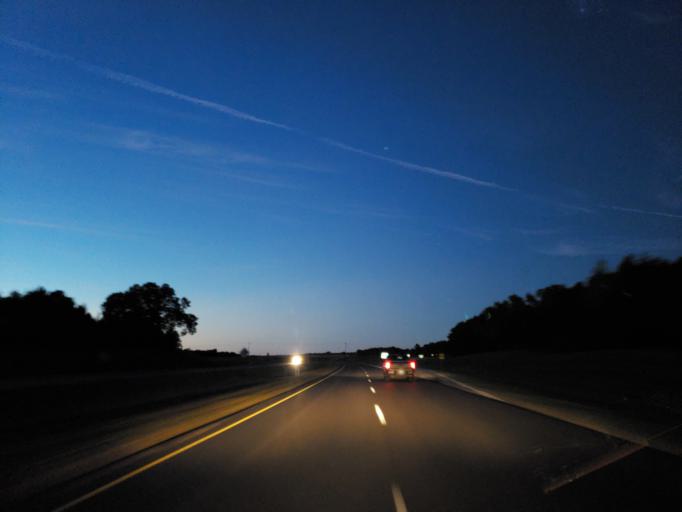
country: US
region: Mississippi
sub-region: Clarke County
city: Quitman
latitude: 32.0539
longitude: -88.6768
